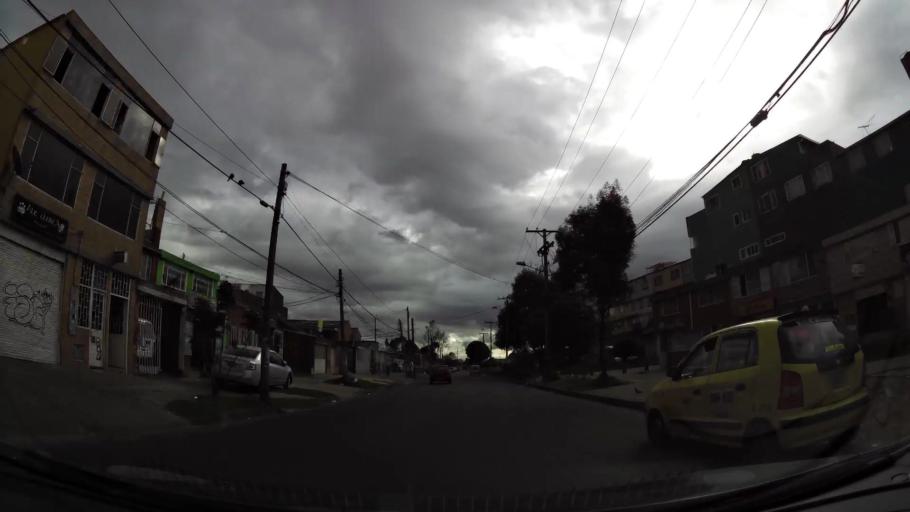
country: CO
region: Bogota D.C.
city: Barrio San Luis
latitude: 4.7094
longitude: -74.1066
